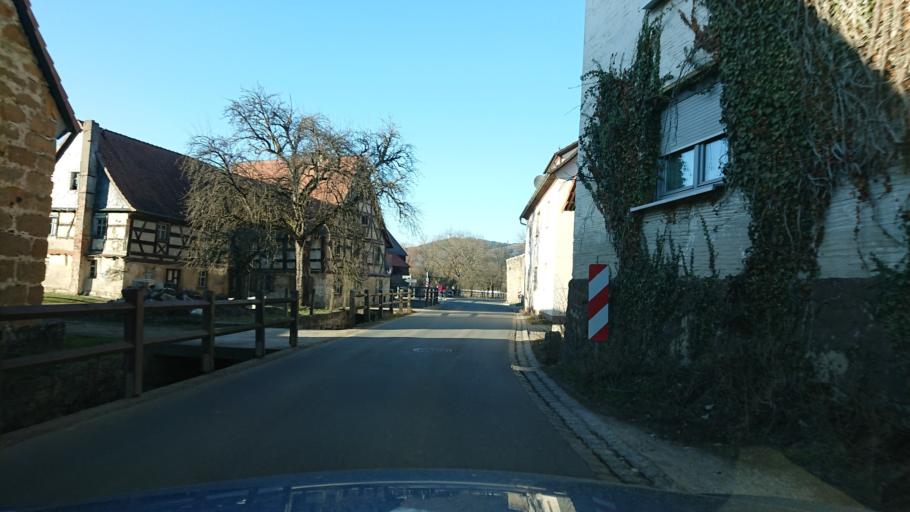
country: DE
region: Bavaria
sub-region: Upper Franconia
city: Pretzfeld
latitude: 49.7567
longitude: 11.1719
